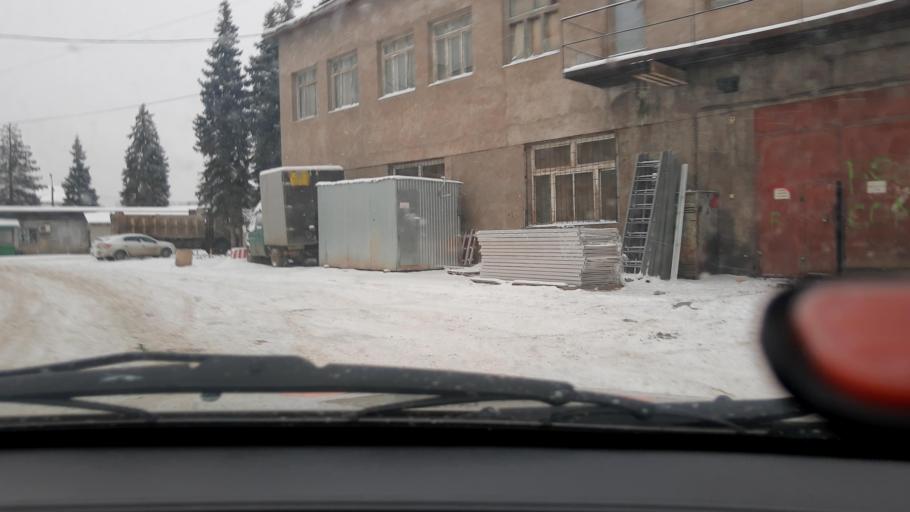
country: RU
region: Bashkortostan
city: Mikhaylovka
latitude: 54.7380
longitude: 55.8967
